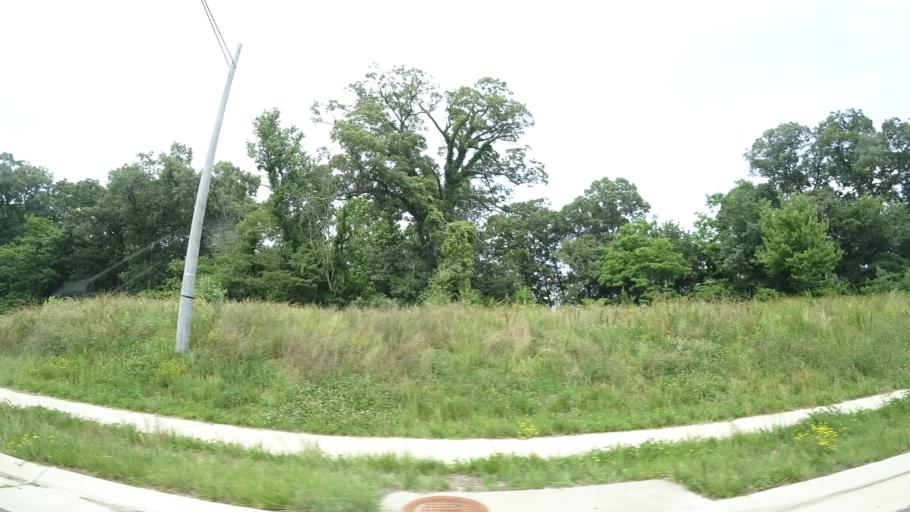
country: US
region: Virginia
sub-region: Fairfax County
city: Lorton
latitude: 38.7049
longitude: -77.2302
